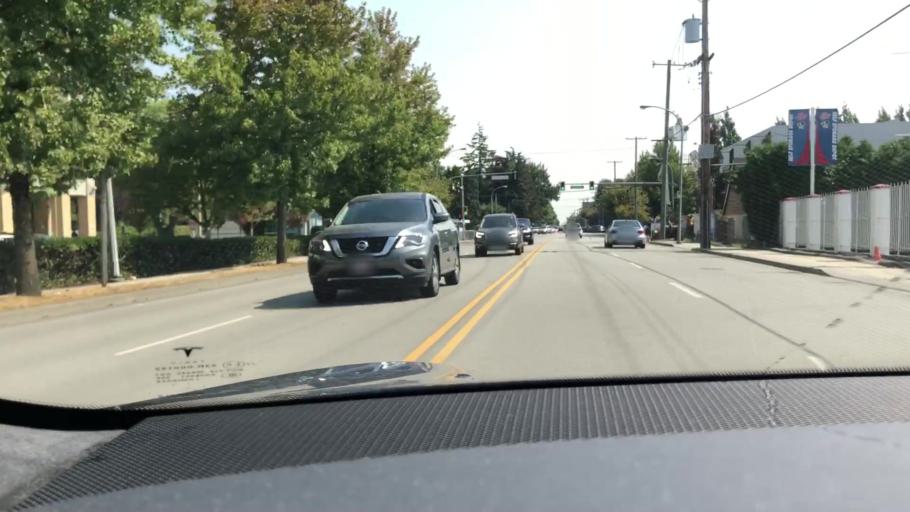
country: CA
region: British Columbia
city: Richmond
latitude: 49.1847
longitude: -123.1296
